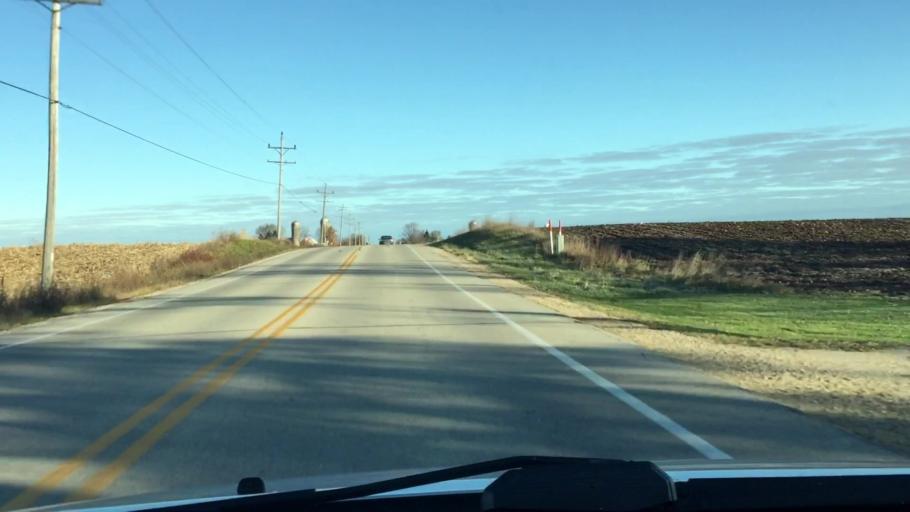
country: US
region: Wisconsin
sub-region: Dodge County
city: Lomira
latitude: 43.6100
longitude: -88.4504
